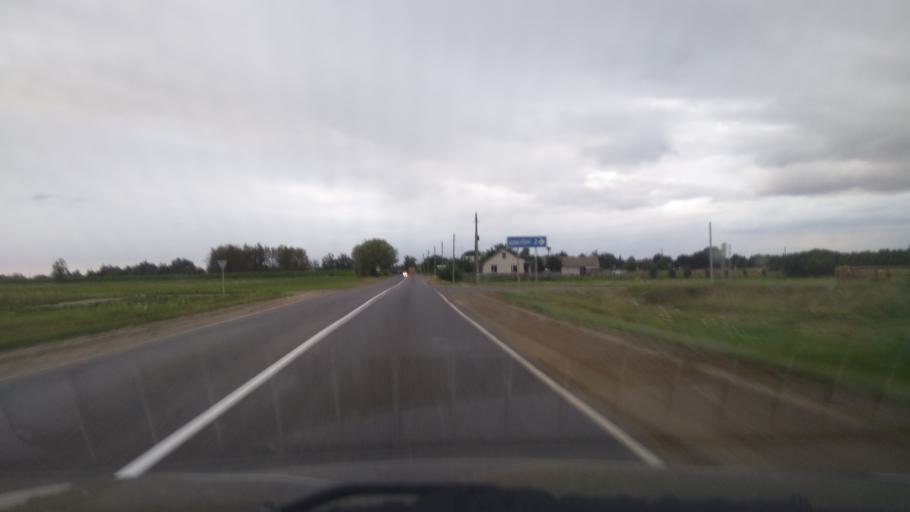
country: BY
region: Brest
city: Byaroza
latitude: 52.4514
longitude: 24.9701
